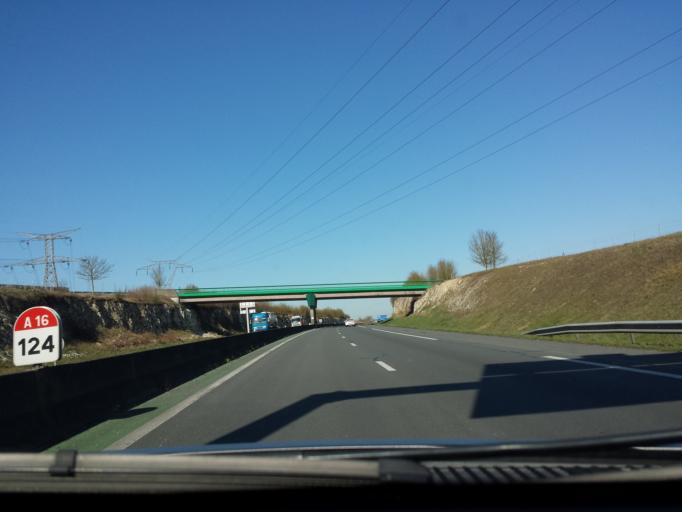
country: FR
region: Picardie
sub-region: Departement de la Somme
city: Saleux
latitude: 49.8678
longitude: 2.2160
